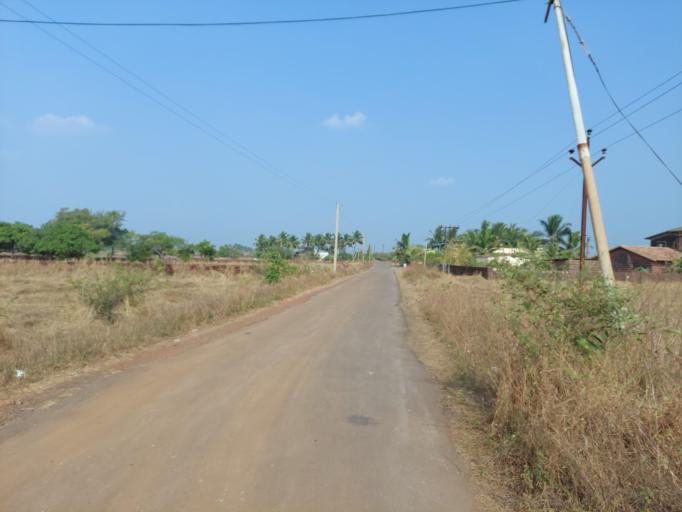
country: IN
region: Maharashtra
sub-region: Ratnagiri
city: Ratnagiri
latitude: 16.9260
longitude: 73.3189
